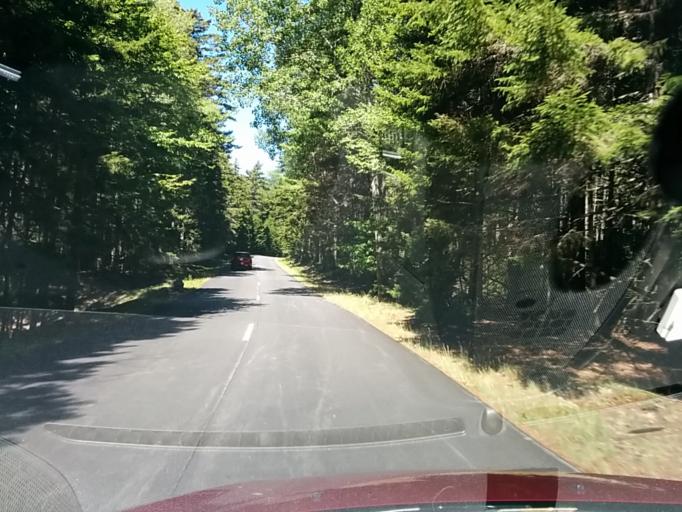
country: US
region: Maine
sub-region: Hancock County
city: Bar Harbor
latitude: 44.3057
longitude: -68.2189
